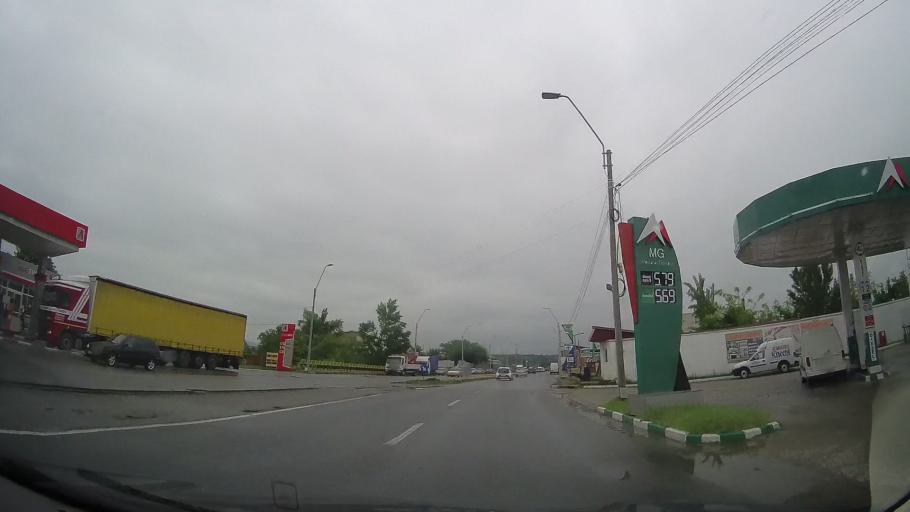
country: RO
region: Mehedinti
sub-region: Comuna Simian
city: Dudasu
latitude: 44.6312
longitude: 22.6849
